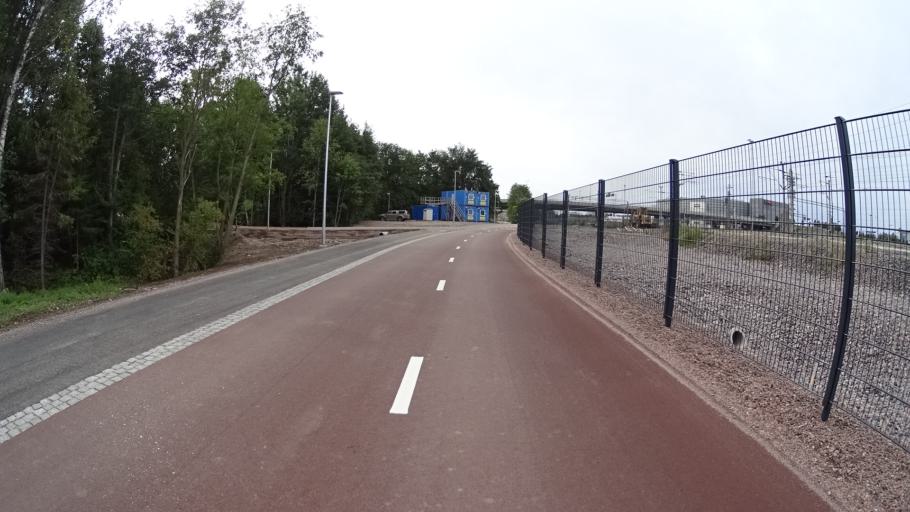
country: FI
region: Uusimaa
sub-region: Helsinki
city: Helsinki
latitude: 60.2084
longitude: 24.9344
